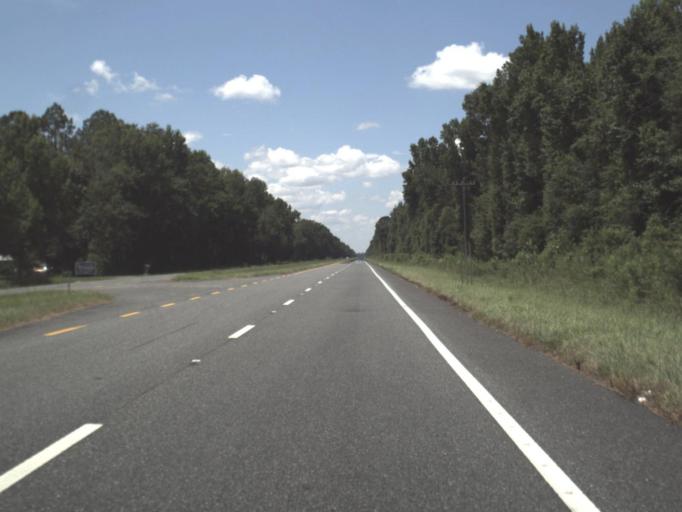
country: US
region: Florida
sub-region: Taylor County
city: Perry
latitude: 30.2788
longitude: -83.7258
